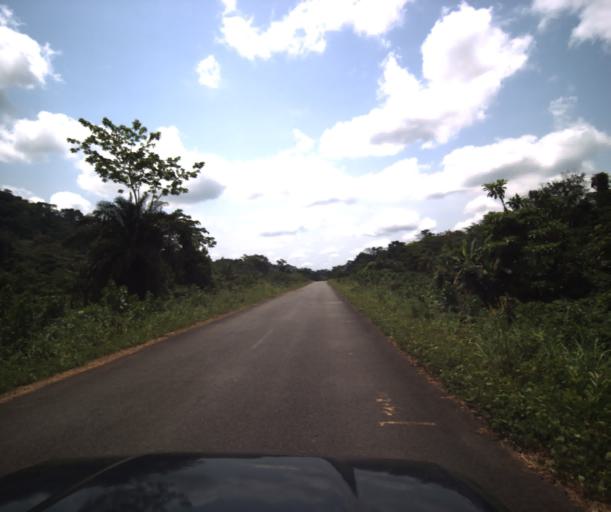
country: CM
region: Centre
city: Eseka
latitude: 3.8166
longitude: 10.8049
